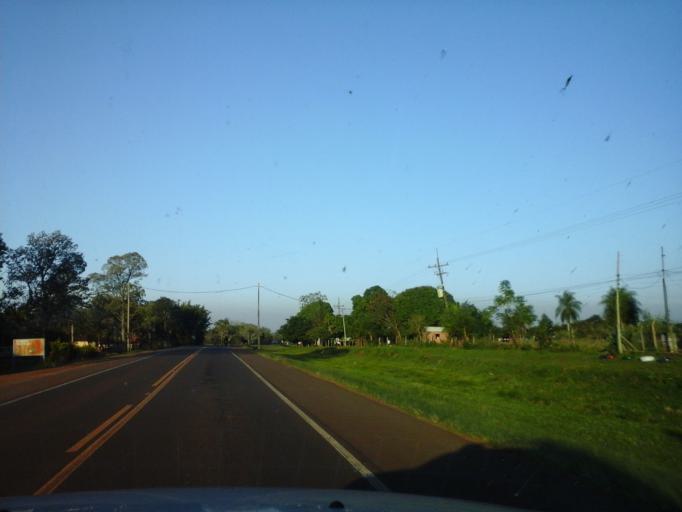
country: PY
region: Itapua
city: General Delgado
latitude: -27.0757
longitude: -56.5791
